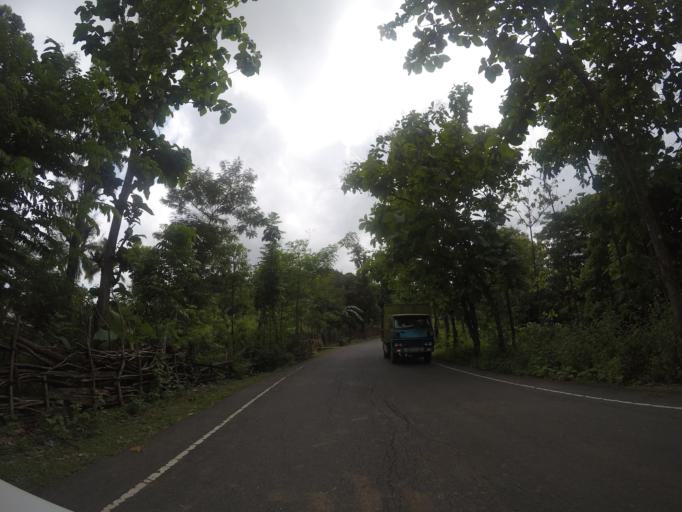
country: TL
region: Bobonaro
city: Maliana
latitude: -8.9533
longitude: 125.0813
